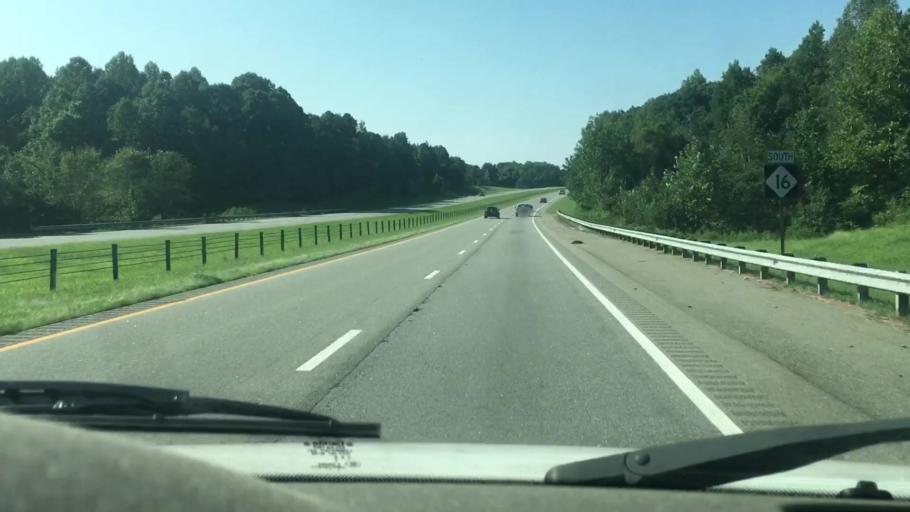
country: US
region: North Carolina
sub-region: Lincoln County
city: Lowesville
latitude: 35.3979
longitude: -80.9981
